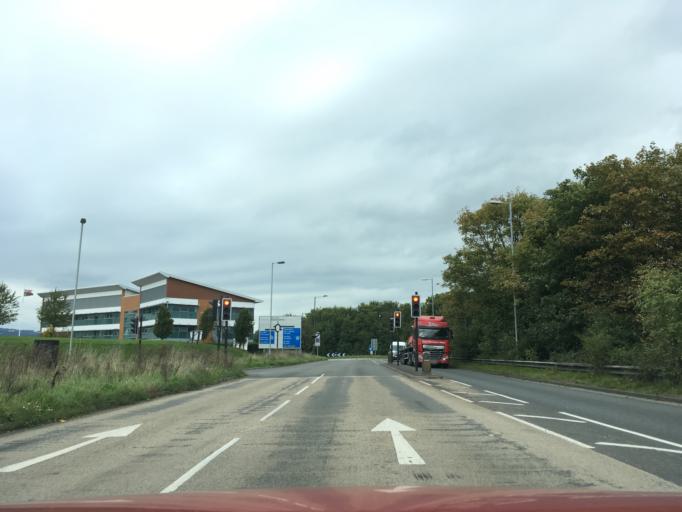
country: GB
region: Wales
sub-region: Monmouthshire
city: Magor
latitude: 51.5852
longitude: -2.8406
